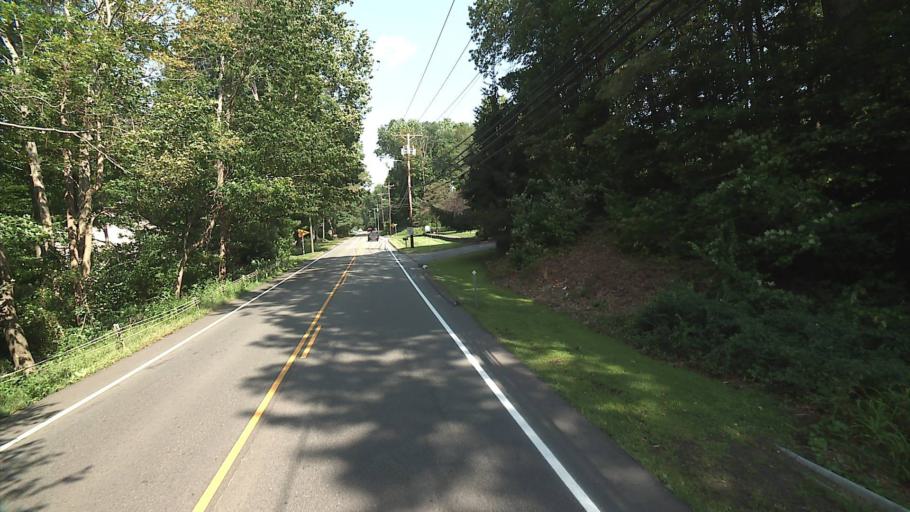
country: US
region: Connecticut
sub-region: New Haven County
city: Madison Center
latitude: 41.2945
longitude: -72.6027
